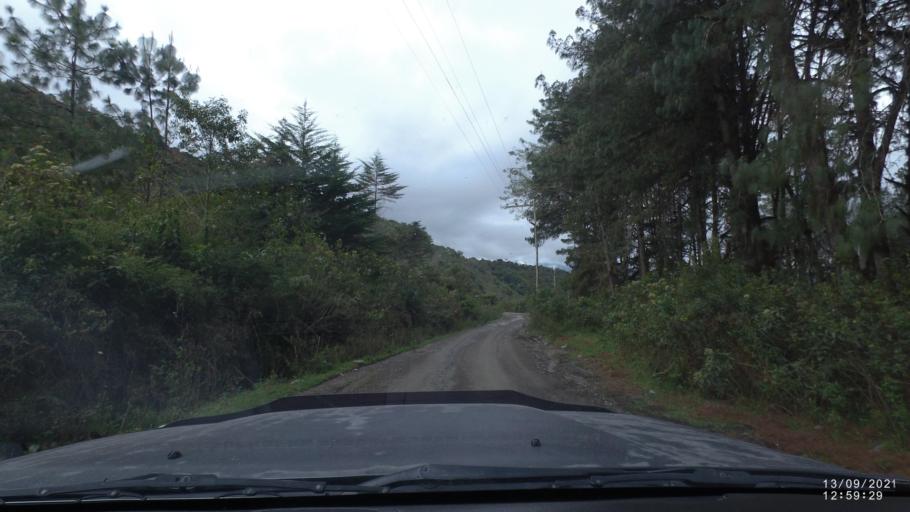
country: BO
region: Cochabamba
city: Colomi
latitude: -17.2347
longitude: -65.8178
